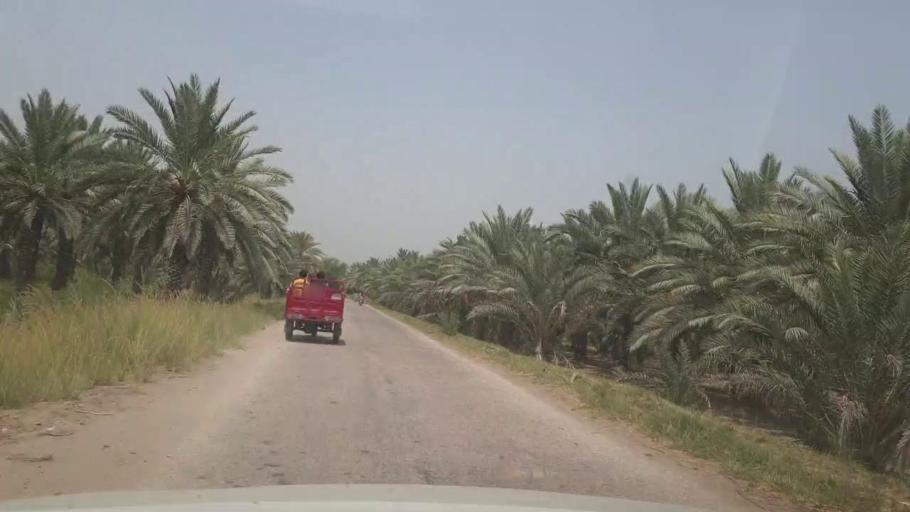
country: PK
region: Sindh
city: Kot Diji
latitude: 27.3631
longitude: 68.6958
